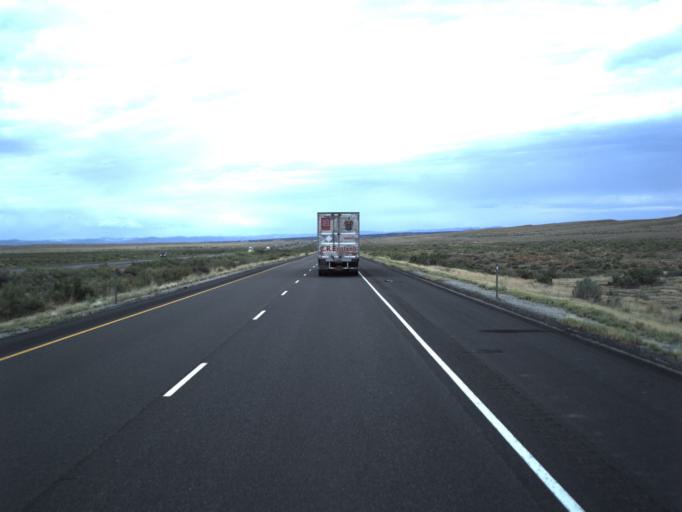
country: US
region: Colorado
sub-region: Mesa County
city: Loma
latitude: 39.0760
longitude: -109.2321
